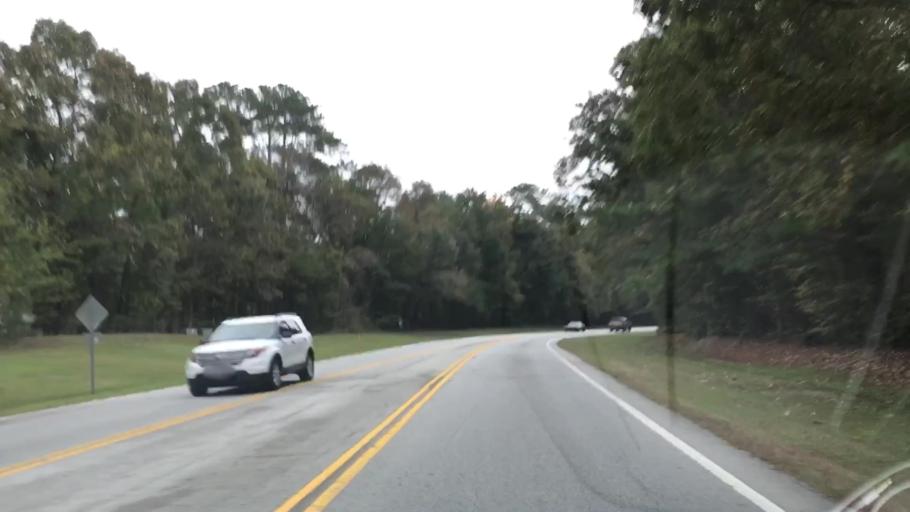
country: US
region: South Carolina
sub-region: Berkeley County
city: Ladson
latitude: 33.0209
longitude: -80.0731
